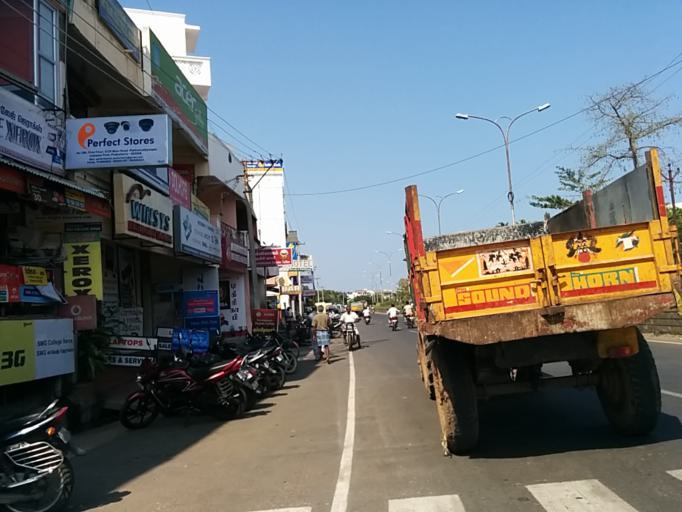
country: IN
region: Pondicherry
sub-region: Puducherry
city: Puducherry
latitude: 11.9441
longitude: 79.8090
